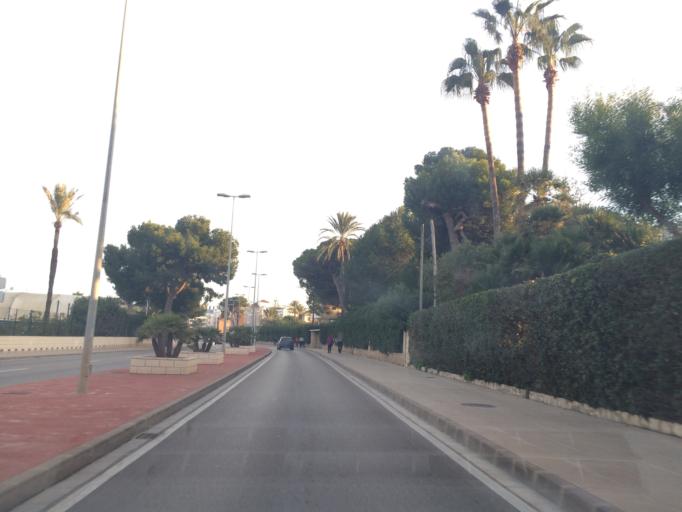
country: ES
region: Valencia
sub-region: Provincia de Alicante
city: Denia
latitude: 38.8384
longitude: 0.1151
